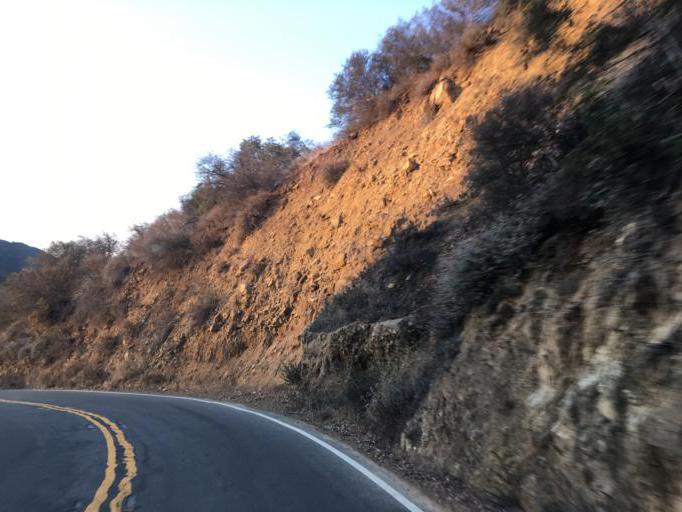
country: US
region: California
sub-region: Los Angeles County
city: Las Flores
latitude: 34.0600
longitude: -118.6397
